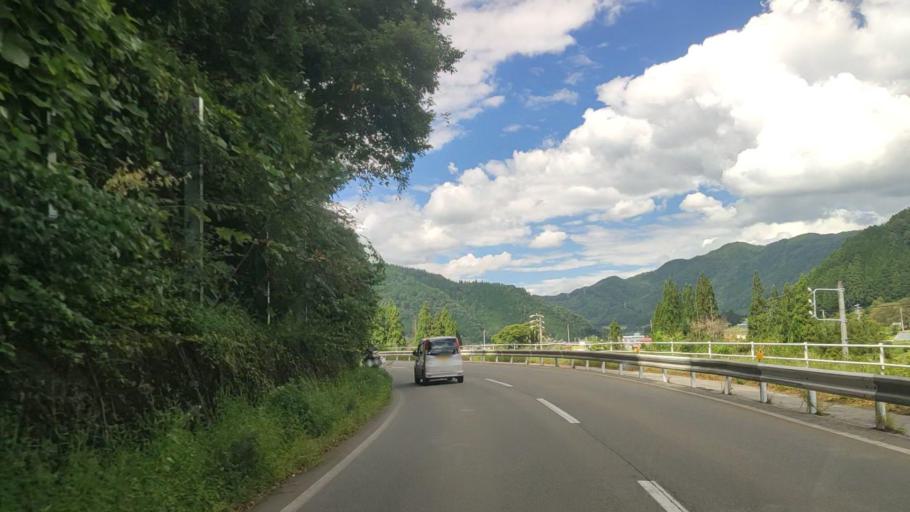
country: JP
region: Gifu
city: Takayama
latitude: 36.1803
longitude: 137.2610
